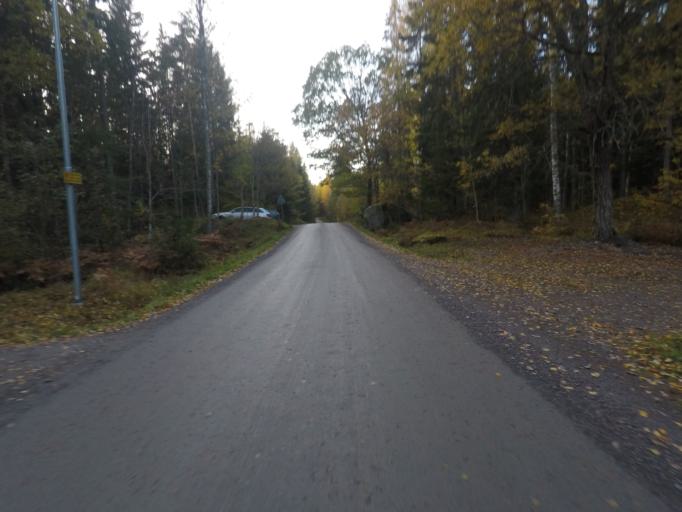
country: SE
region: OErebro
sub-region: Karlskoga Kommun
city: Karlskoga
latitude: 59.3010
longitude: 14.5061
